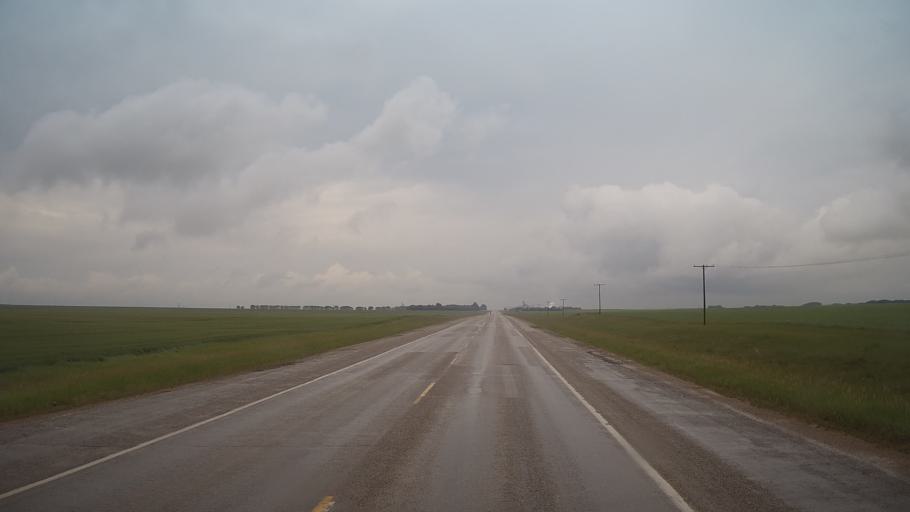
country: CA
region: Saskatchewan
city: Unity
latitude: 52.4350
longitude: -109.0618
